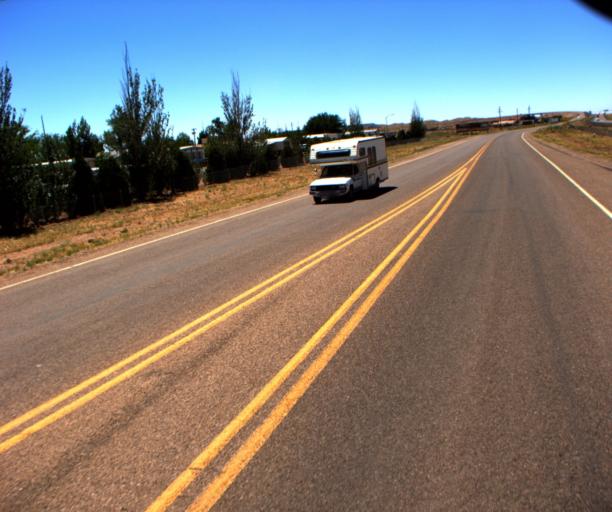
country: US
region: Arizona
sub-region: Coconino County
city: LeChee
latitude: 35.0378
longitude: -110.7301
